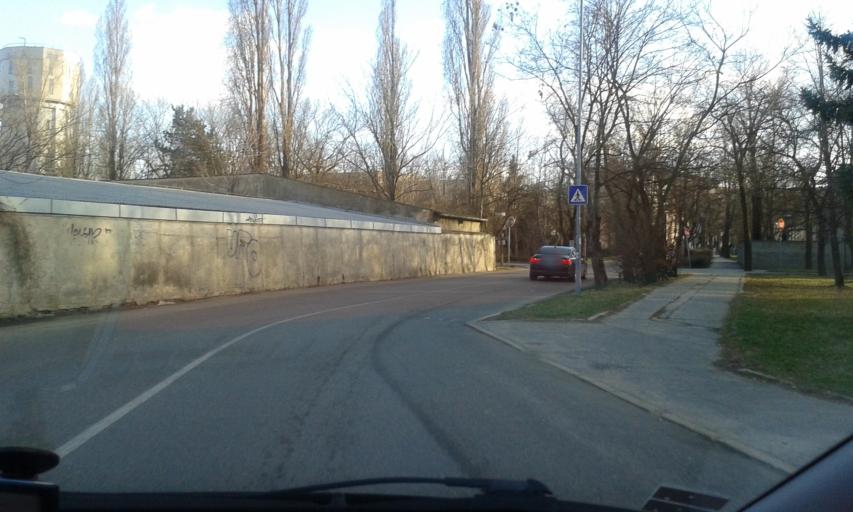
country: SK
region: Bratislavsky
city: Bratislava
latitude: 48.1859
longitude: 17.1373
